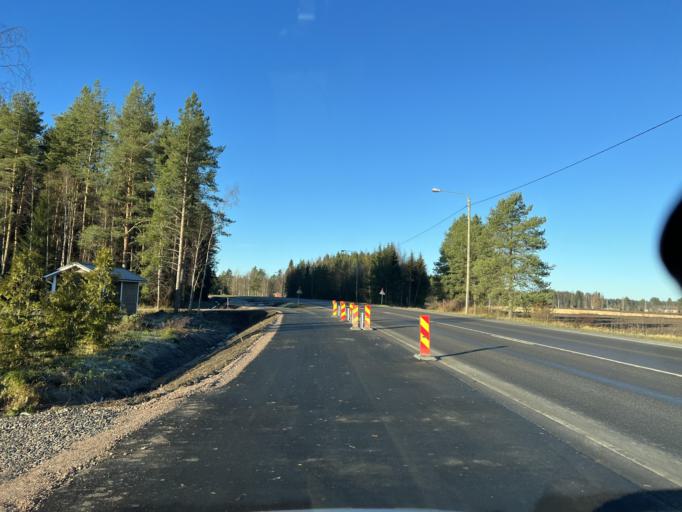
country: FI
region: Northern Ostrobothnia
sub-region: Nivala-Haapajaervi
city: Nivala
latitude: 63.9496
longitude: 24.9203
